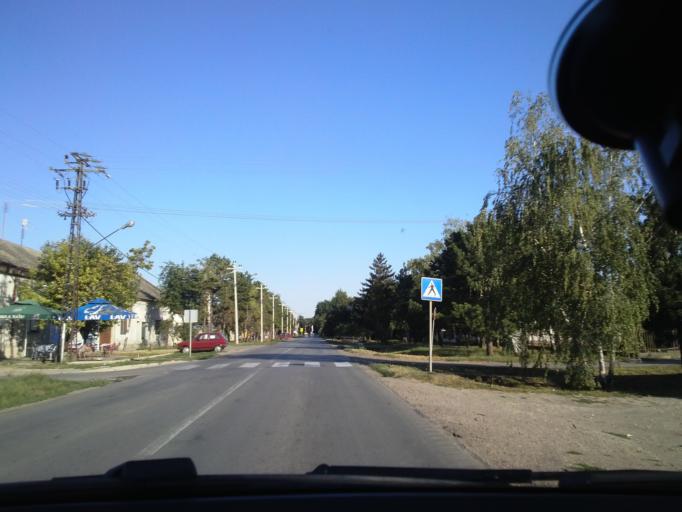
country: RS
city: Doroslovo
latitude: 45.6666
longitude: 19.1973
